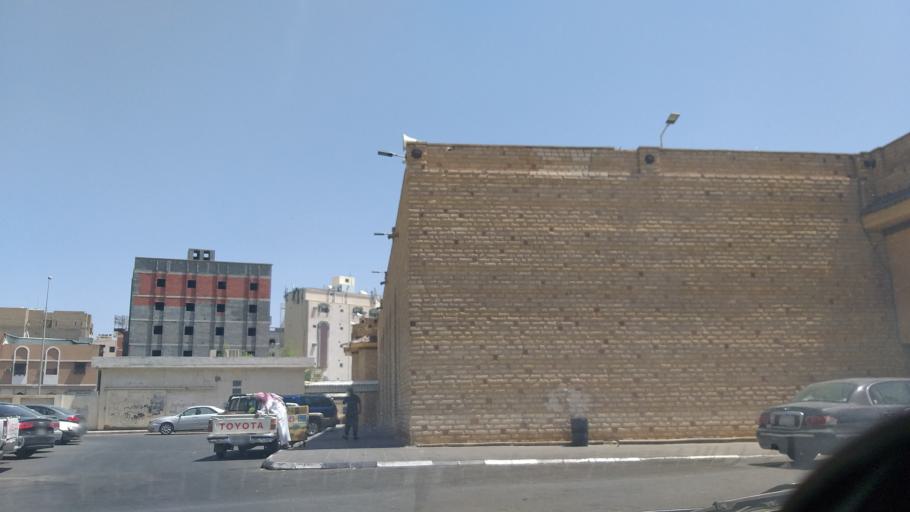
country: SA
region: Makkah
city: Ta'if
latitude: 21.2700
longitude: 40.4076
